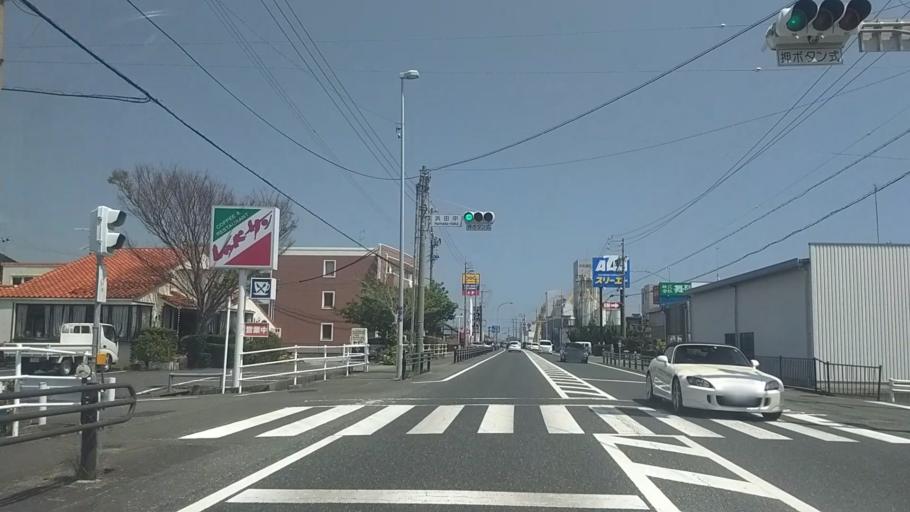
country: JP
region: Shizuoka
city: Kosai-shi
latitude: 34.6820
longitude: 137.6248
